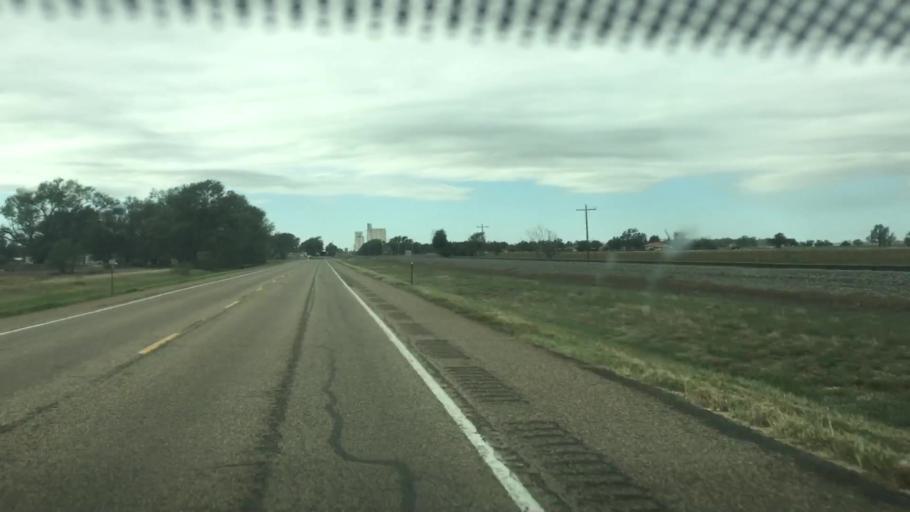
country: US
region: Colorado
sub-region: Prowers County
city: Lamar
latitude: 38.0602
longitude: -102.2950
